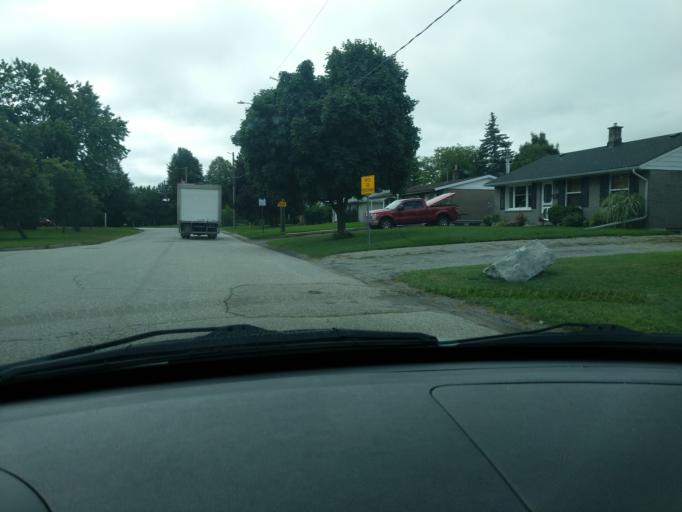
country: CA
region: Ontario
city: Cambridge
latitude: 43.4209
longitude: -80.3162
